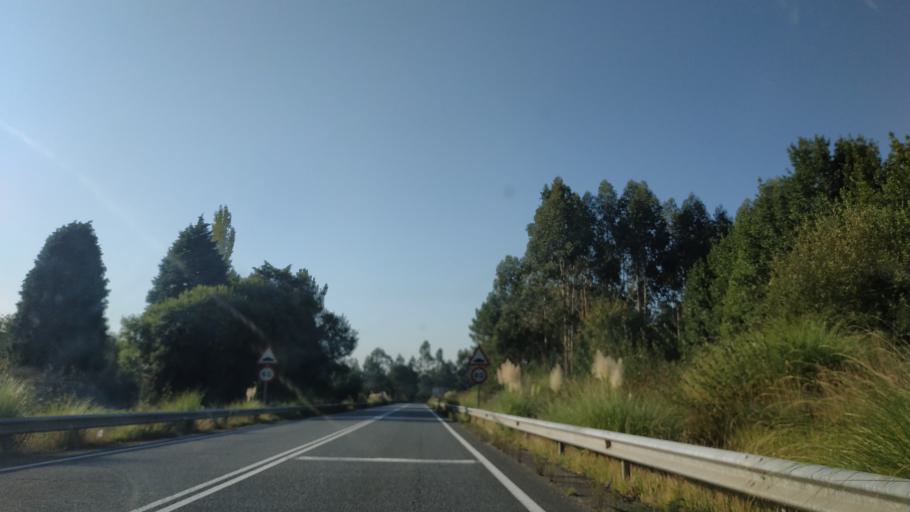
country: ES
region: Galicia
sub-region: Provincia da Coruna
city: Carballo
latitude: 43.2350
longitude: -8.6782
